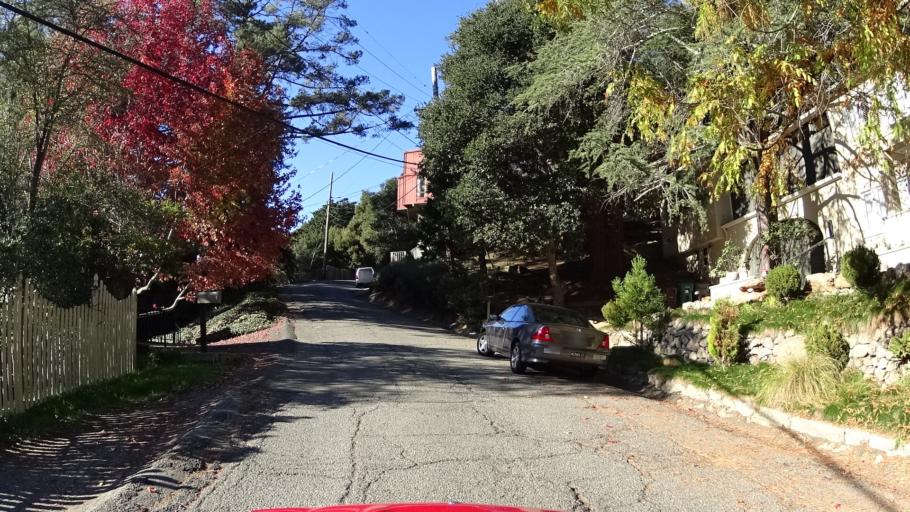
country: US
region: California
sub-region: Alameda County
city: Piedmont
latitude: 37.8369
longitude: -122.2083
